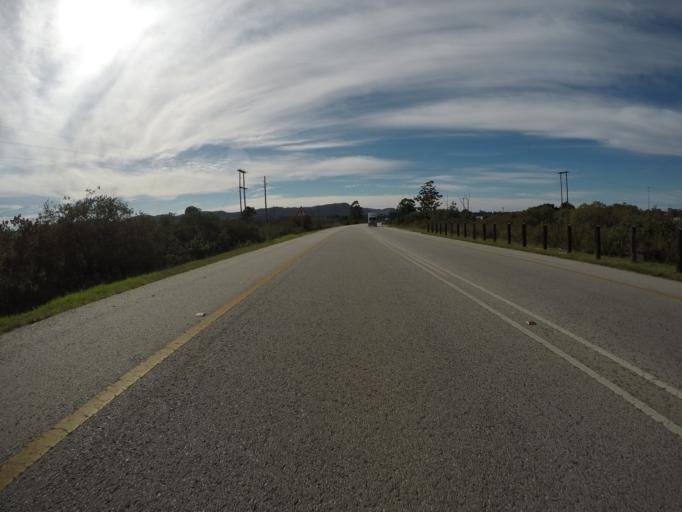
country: ZA
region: Eastern Cape
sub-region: Cacadu District Municipality
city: Jeffrey's Bay
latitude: -33.8921
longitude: 25.1354
